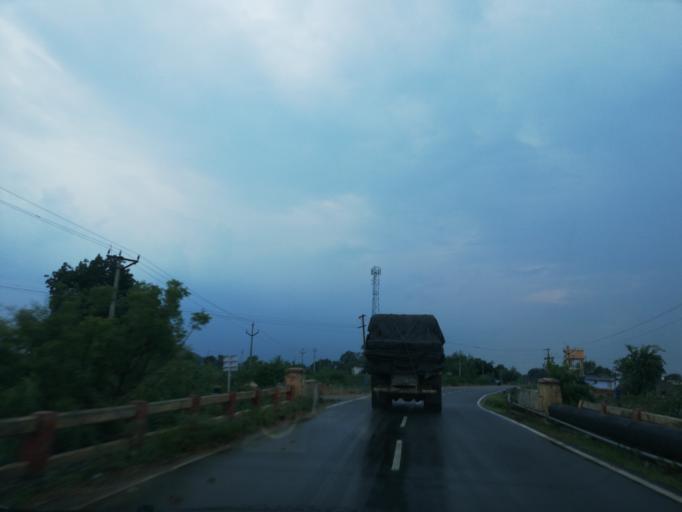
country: IN
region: Andhra Pradesh
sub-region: Guntur
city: Macherla
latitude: 16.6758
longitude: 79.2668
